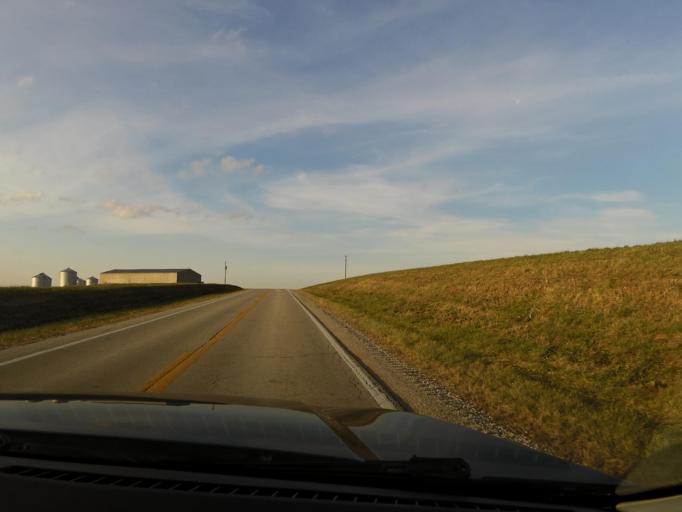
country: US
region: Illinois
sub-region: Fayette County
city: Vandalia
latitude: 38.9495
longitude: -89.1453
